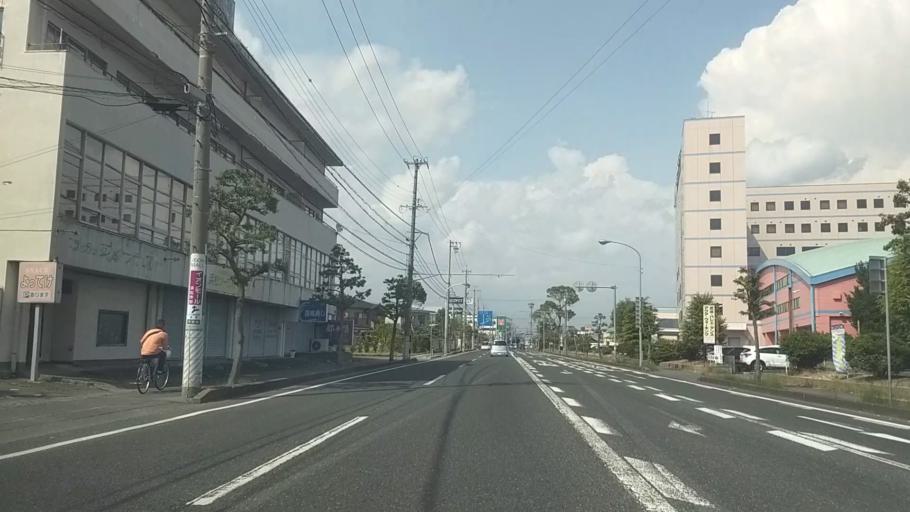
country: JP
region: Shizuoka
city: Hamamatsu
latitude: 34.7165
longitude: 137.7620
